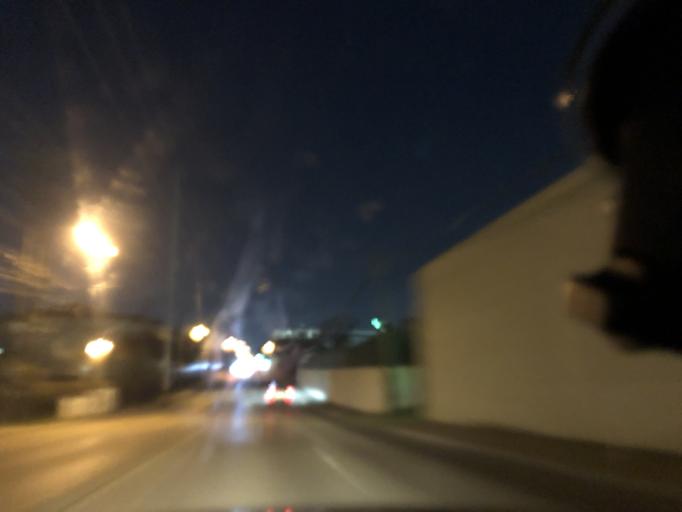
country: US
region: Texas
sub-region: Dallas County
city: University Park
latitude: 32.8257
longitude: -96.8417
